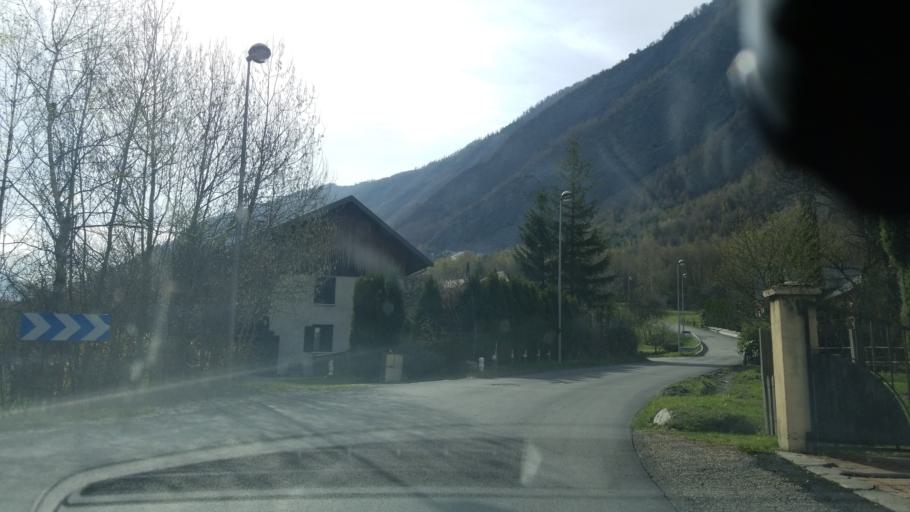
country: FR
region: Rhone-Alpes
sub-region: Departement de la Savoie
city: Villargondran
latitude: 45.2521
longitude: 6.3889
